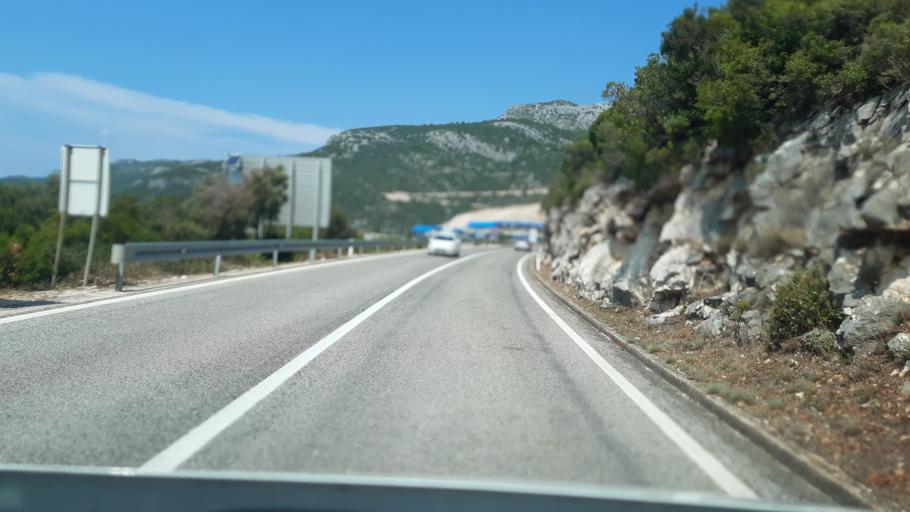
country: BA
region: Federation of Bosnia and Herzegovina
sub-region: Hercegovacko-Bosanski Kanton
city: Neum
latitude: 42.9364
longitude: 17.5829
